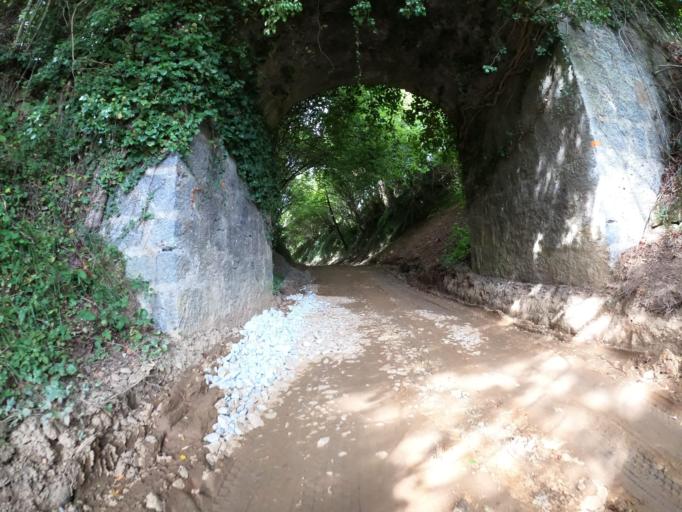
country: ES
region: Navarre
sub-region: Provincia de Navarra
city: Lekunberri
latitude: 43.0104
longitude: -1.8929
